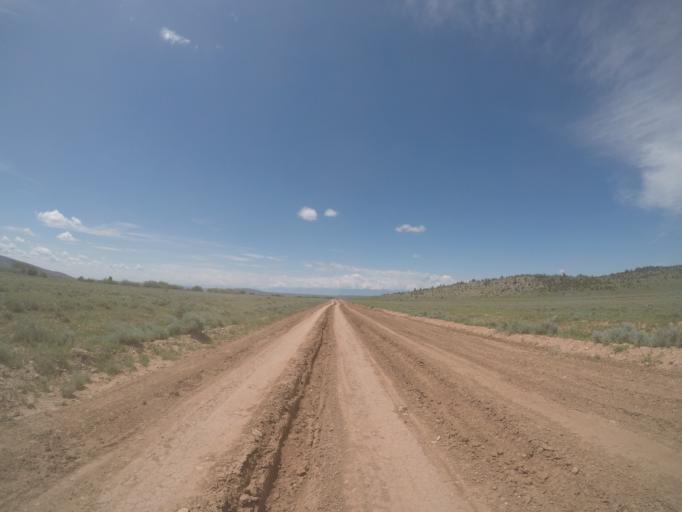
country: US
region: Montana
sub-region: Yellowstone County
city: Laurel
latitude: 45.2427
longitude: -108.6643
